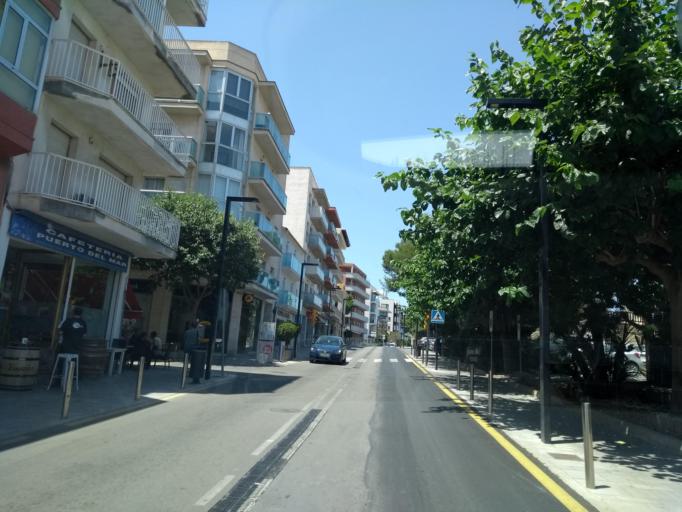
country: ES
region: Balearic Islands
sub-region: Illes Balears
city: Port d'Alcudia
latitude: 39.8415
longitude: 3.1361
